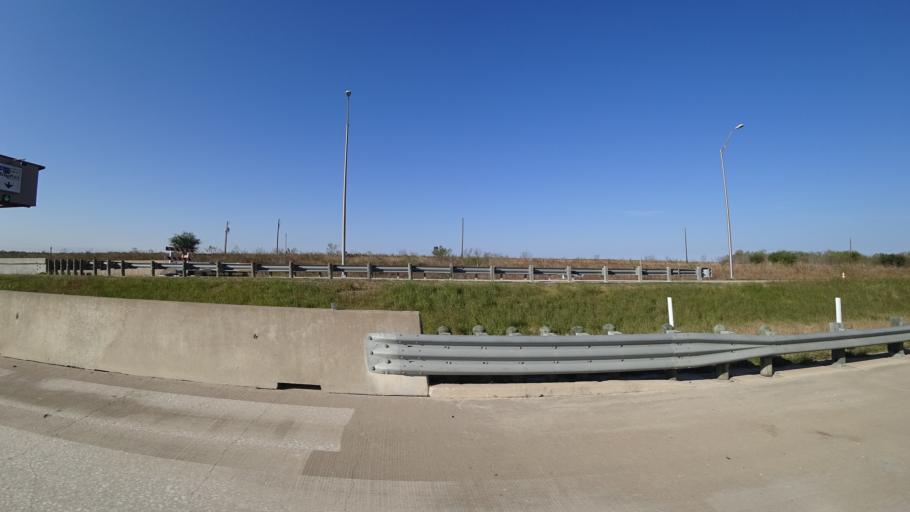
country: US
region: Texas
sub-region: Travis County
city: Onion Creek
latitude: 30.1344
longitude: -97.6666
